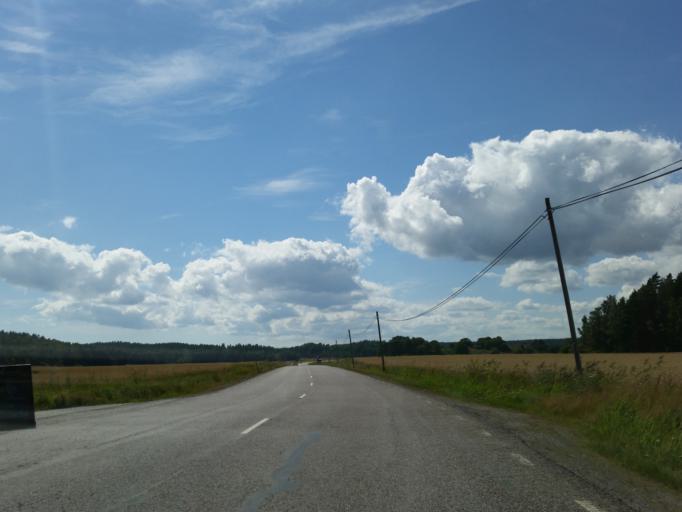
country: SE
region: Soedermanland
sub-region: Trosa Kommun
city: Vagnharad
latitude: 58.9914
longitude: 17.6445
